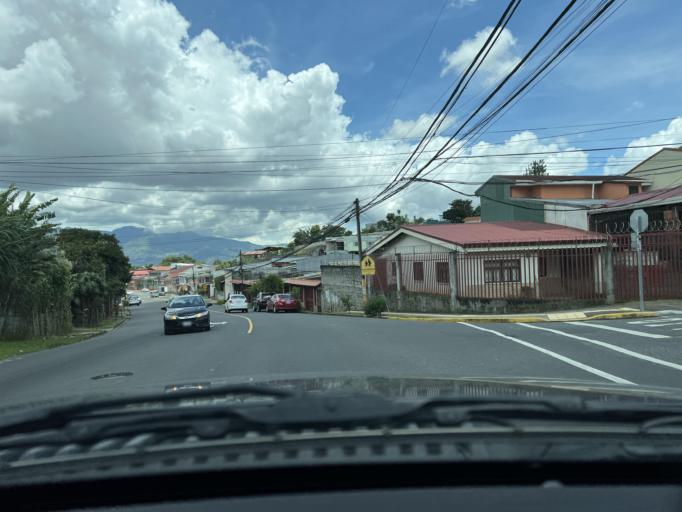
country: CR
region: San Jose
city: Granadilla
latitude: 9.9432
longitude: -84.0258
